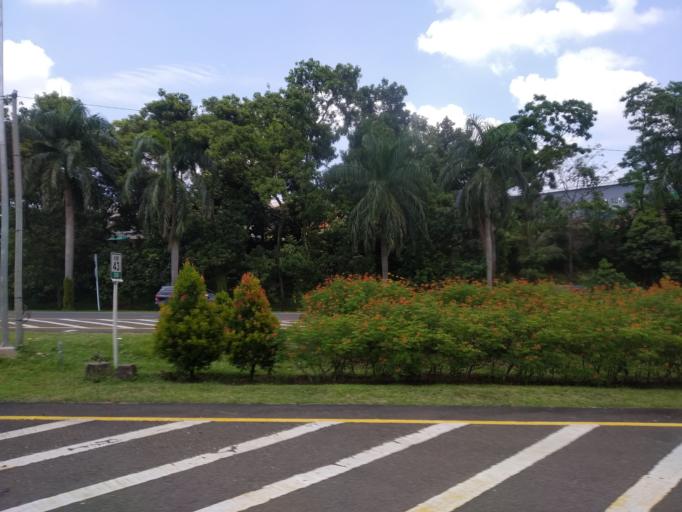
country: ID
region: West Java
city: Bogor
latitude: -6.6017
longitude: 106.8113
